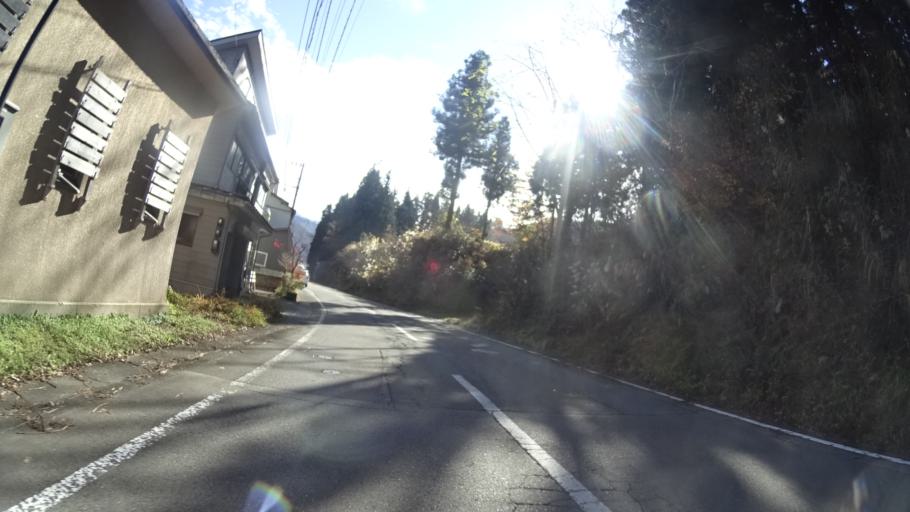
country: JP
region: Niigata
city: Muikamachi
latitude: 37.1964
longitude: 139.0773
